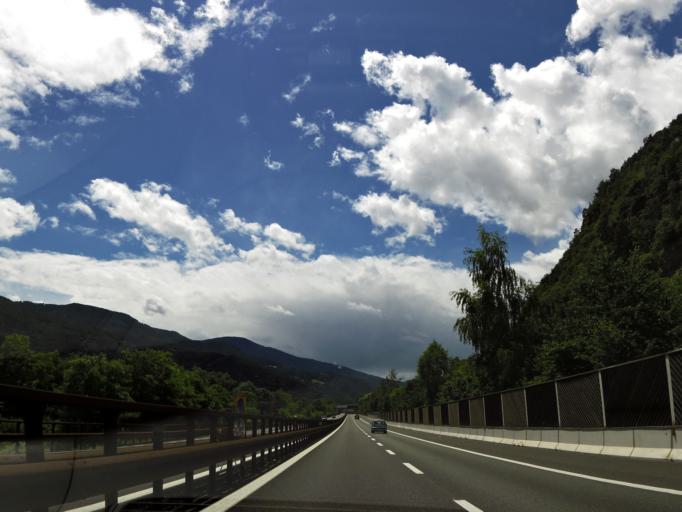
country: IT
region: Trentino-Alto Adige
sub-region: Bolzano
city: Bressanone
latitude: 46.6998
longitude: 11.6455
